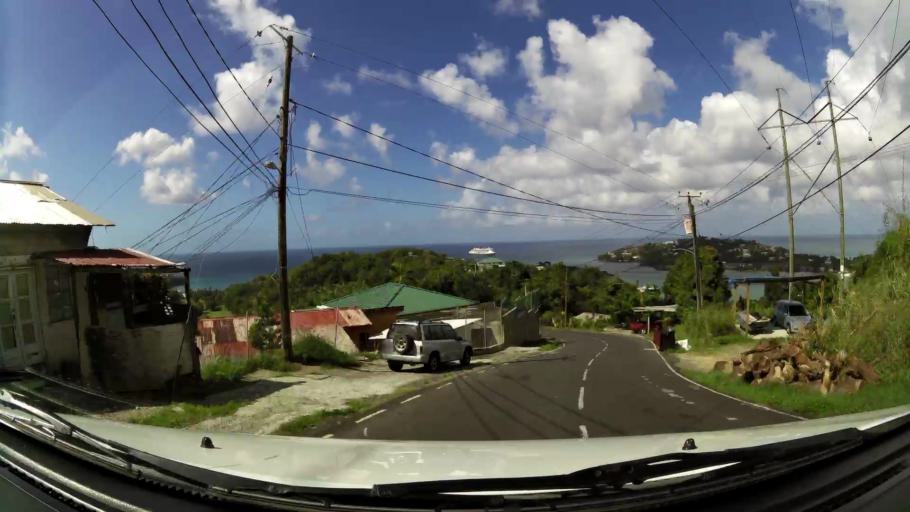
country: LC
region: Castries Quarter
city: Castries
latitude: 14.0055
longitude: -60.9999
